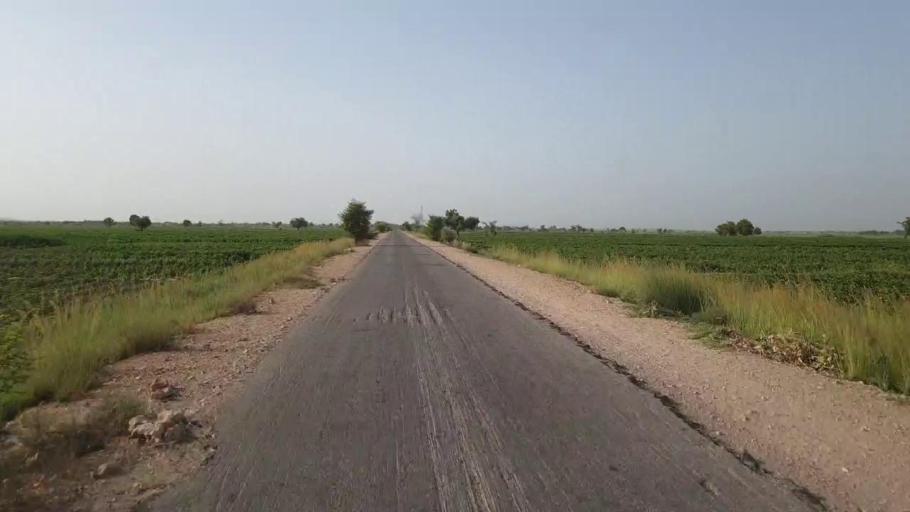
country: PK
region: Sindh
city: Jam Sahib
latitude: 26.4708
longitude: 68.8594
